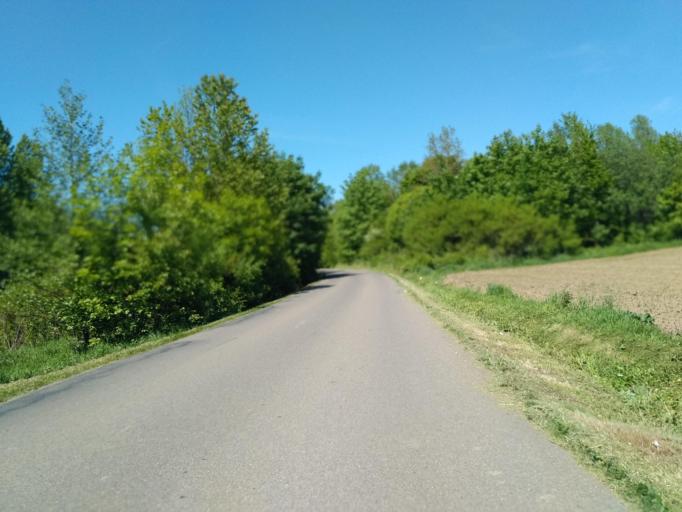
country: PL
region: Subcarpathian Voivodeship
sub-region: Powiat brzozowski
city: Gorki
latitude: 49.6624
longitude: 22.0296
